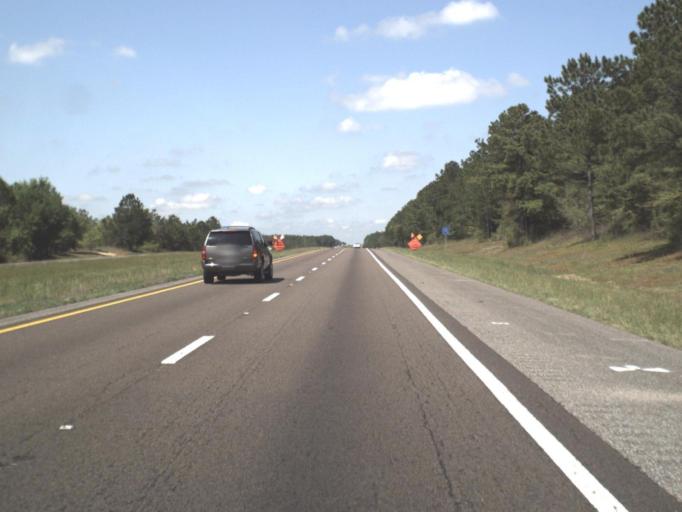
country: US
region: Florida
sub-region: Santa Rosa County
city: East Milton
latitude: 30.6831
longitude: -86.8002
